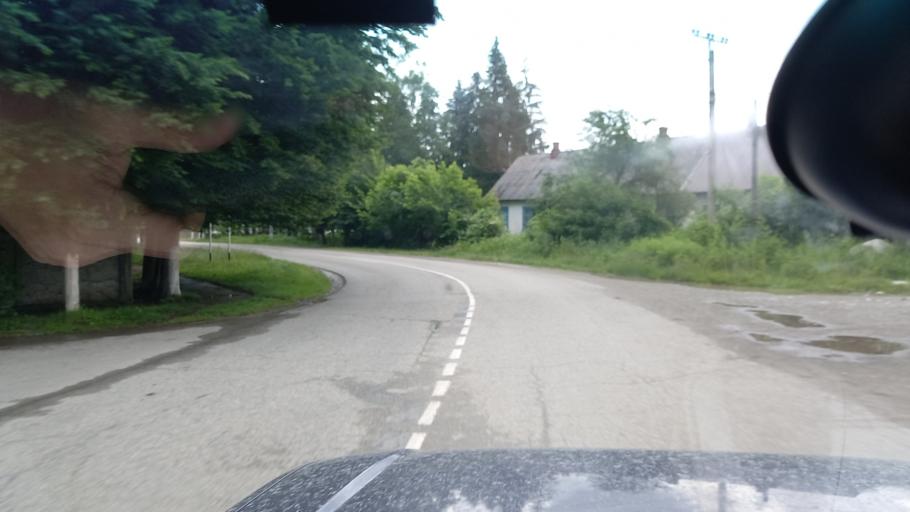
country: RU
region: Krasnodarskiy
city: Psebay
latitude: 44.0474
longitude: 40.7640
